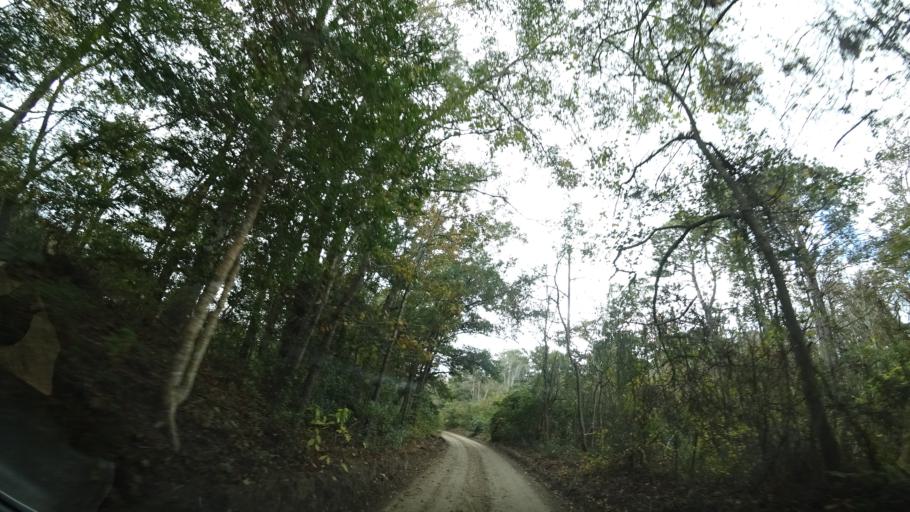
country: US
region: North Carolina
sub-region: Dare County
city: Kill Devil Hills
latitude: 35.9943
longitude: -75.6663
